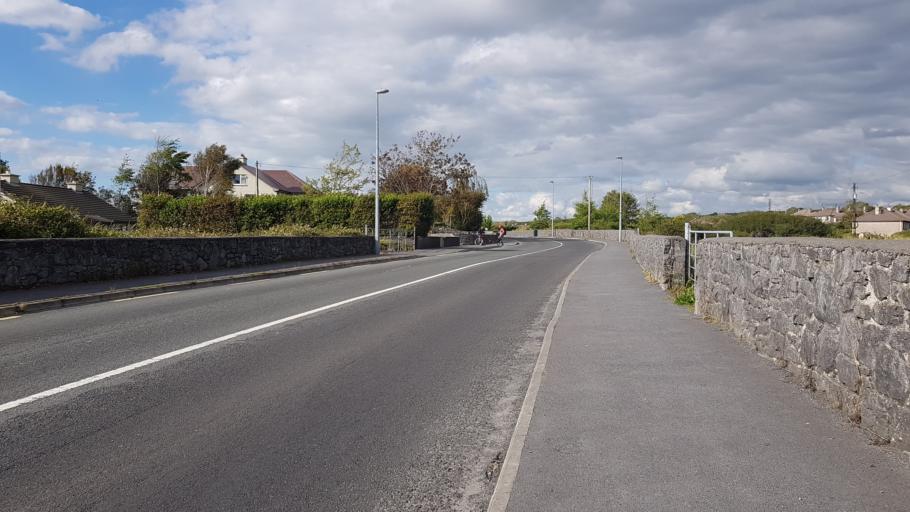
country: IE
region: Connaught
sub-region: County Galway
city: Gaillimh
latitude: 53.2899
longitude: -9.0521
